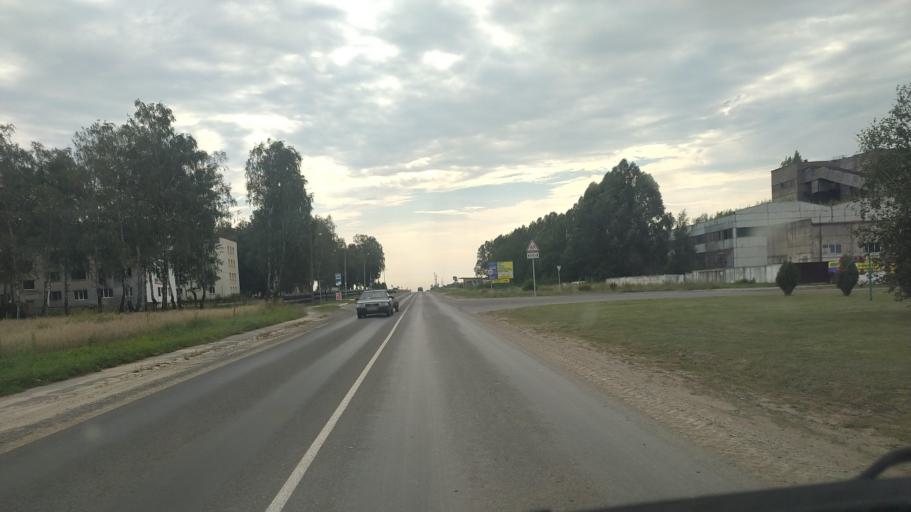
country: BY
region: Brest
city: Byaroza
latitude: 52.5519
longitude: 24.9348
